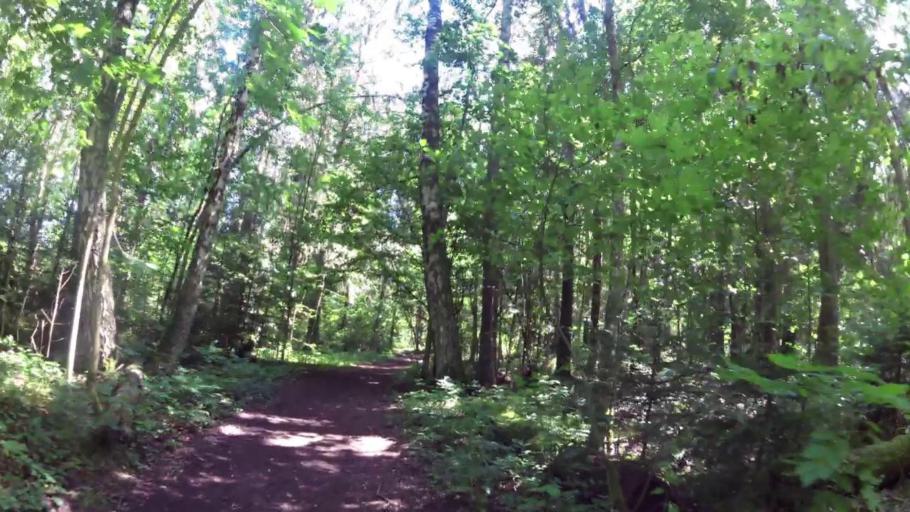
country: SE
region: OEstergoetland
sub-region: Linkopings Kommun
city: Linkoping
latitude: 58.4021
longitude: 15.5945
